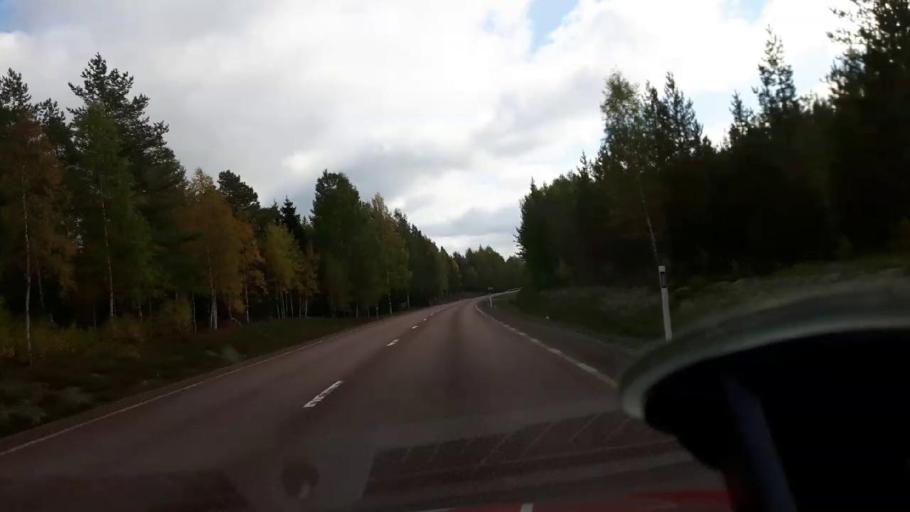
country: SE
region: Gaevleborg
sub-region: Ljusdals Kommun
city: Jaervsoe
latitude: 61.6362
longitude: 16.2603
